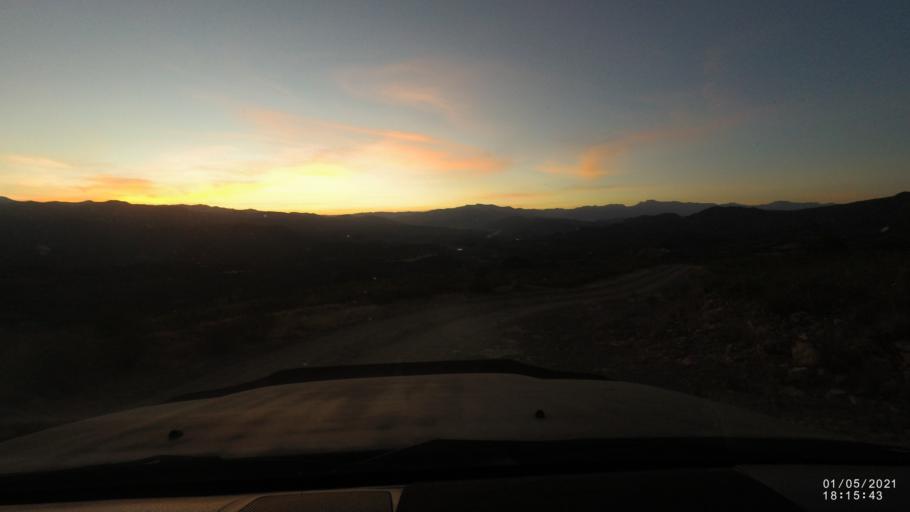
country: BO
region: Cochabamba
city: Capinota
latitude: -17.6752
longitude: -66.2172
